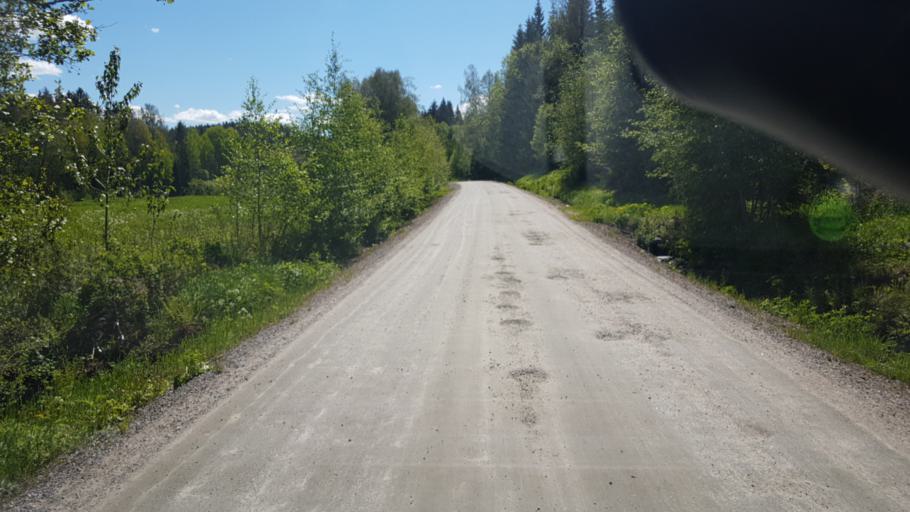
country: SE
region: Vaermland
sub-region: Arvika Kommun
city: Arvika
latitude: 59.6654
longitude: 12.7588
